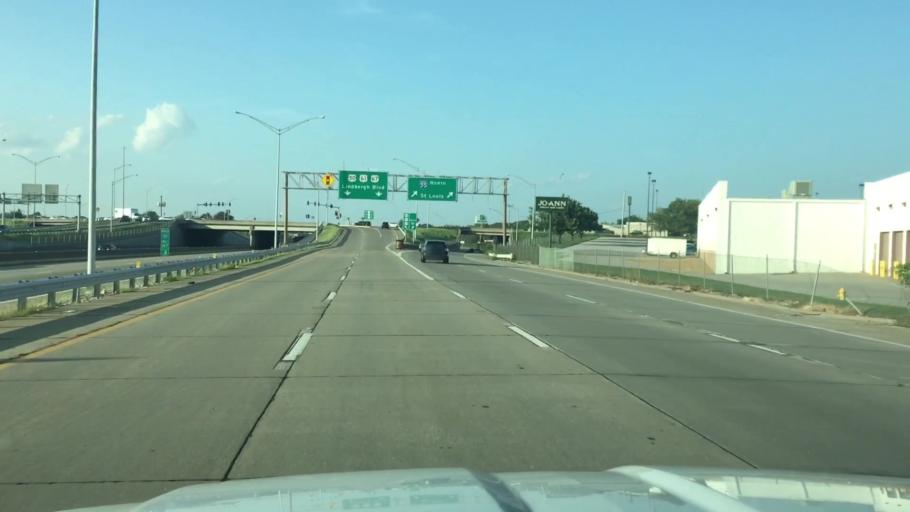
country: US
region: Missouri
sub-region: Saint Louis County
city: Mehlville
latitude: 38.5087
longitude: -90.3363
